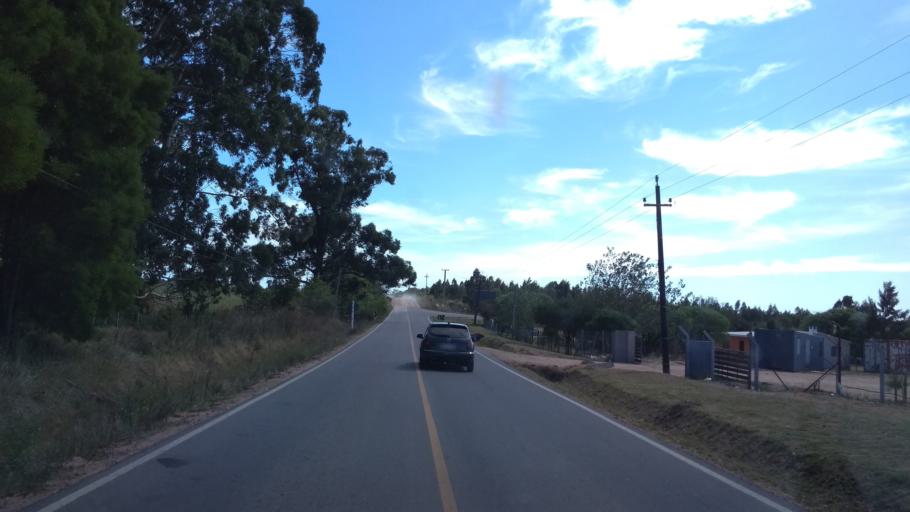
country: UY
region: Canelones
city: Joaquin Suarez
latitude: -34.7190
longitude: -56.0258
